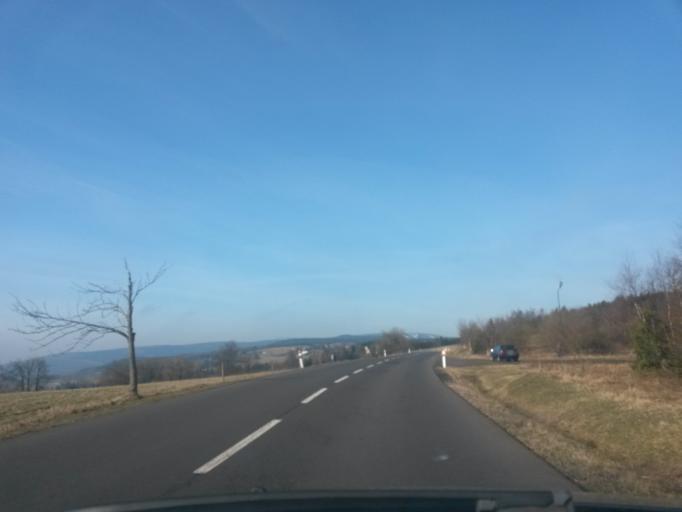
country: CZ
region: Ustecky
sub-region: Okres Chomutov
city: Perstejn
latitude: 50.4198
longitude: 13.0997
